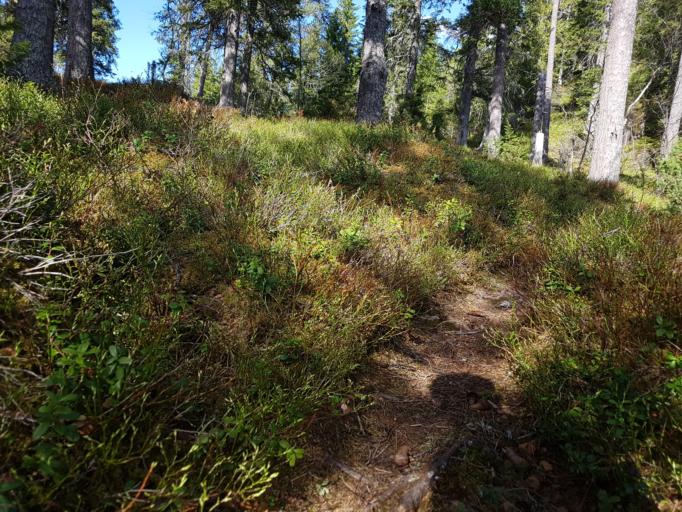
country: NO
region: Sor-Trondelag
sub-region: Trondheim
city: Trondheim
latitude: 63.4397
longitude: 10.2916
